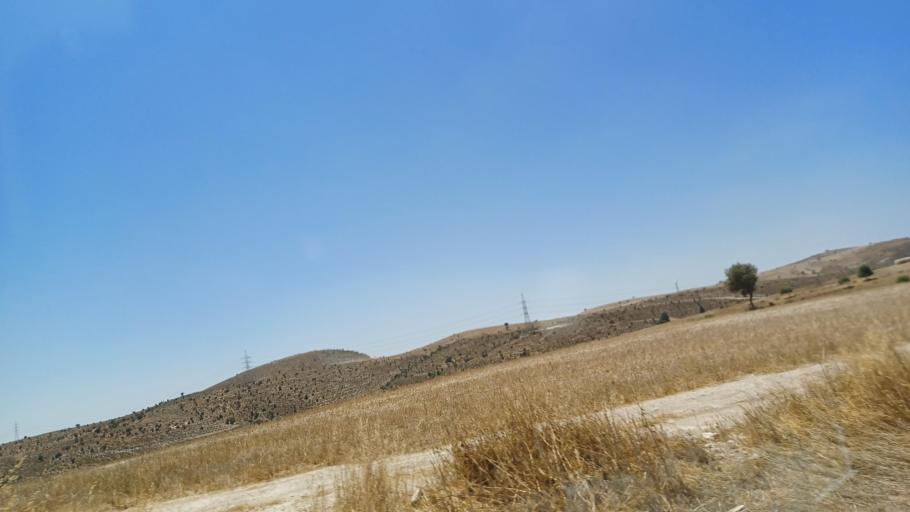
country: CY
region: Lefkosia
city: Lympia
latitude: 34.9901
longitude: 33.4778
